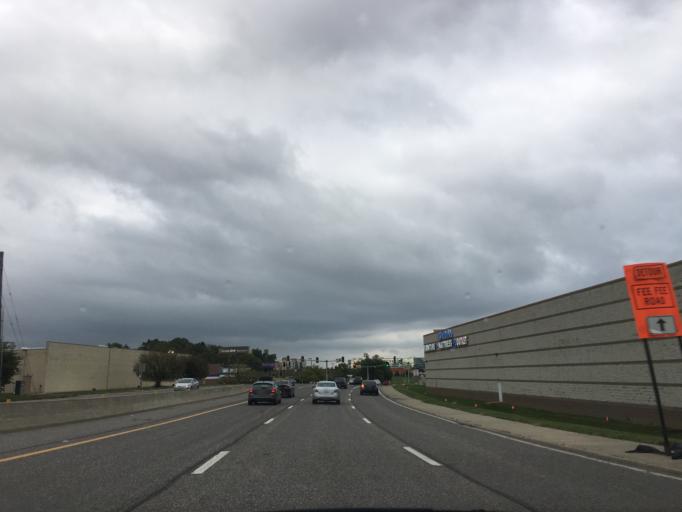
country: US
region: Missouri
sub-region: Saint Louis County
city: Saint Ann
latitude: 38.7335
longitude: -90.4036
